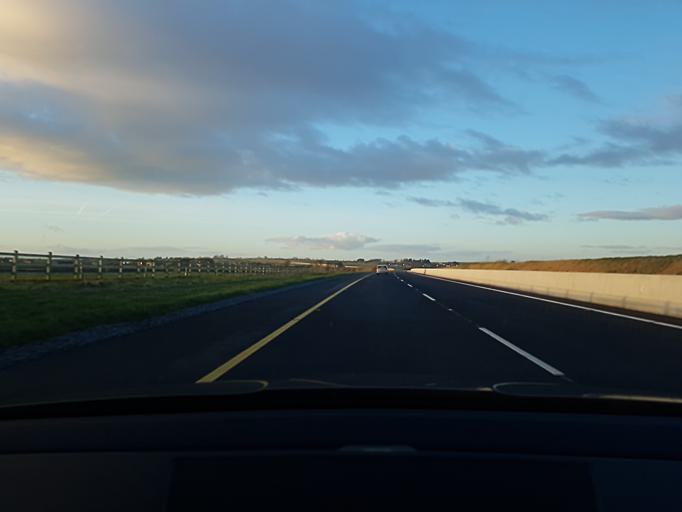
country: IE
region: Connaught
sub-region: County Galway
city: Athenry
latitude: 53.3845
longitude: -8.8001
